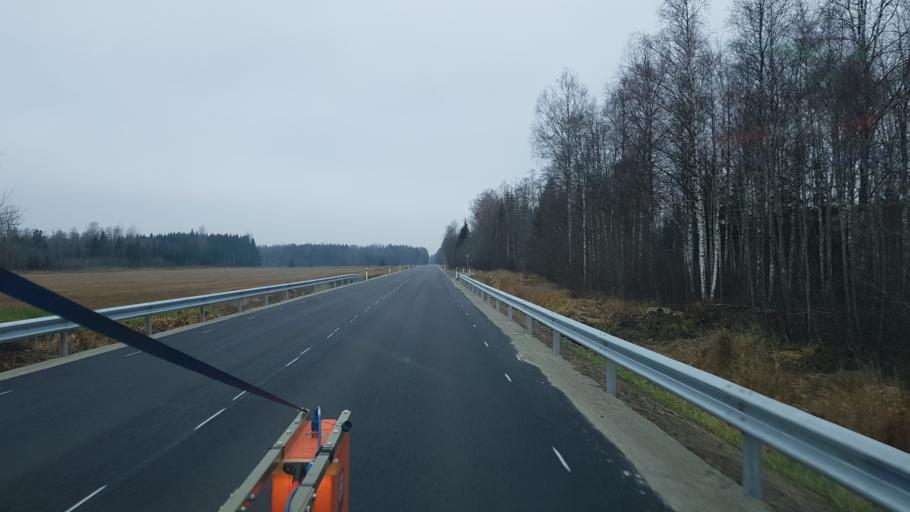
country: EE
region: Paernumaa
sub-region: Vaendra vald (alev)
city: Vandra
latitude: 58.8387
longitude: 25.0726
